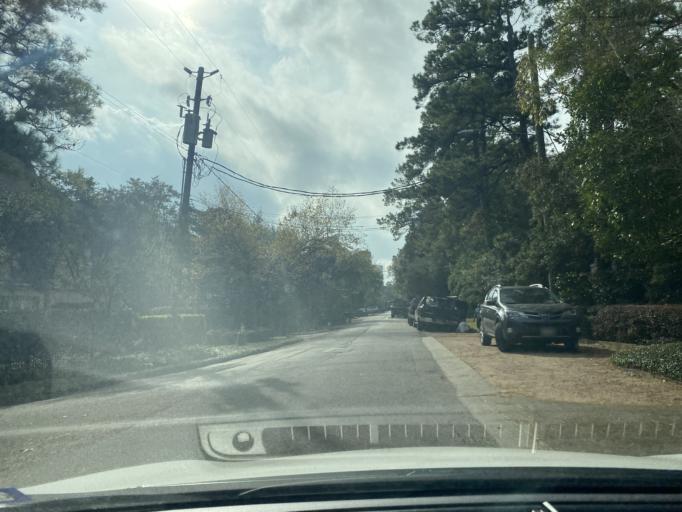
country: US
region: Texas
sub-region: Harris County
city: Hunters Creek Village
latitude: 29.7692
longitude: -95.4734
